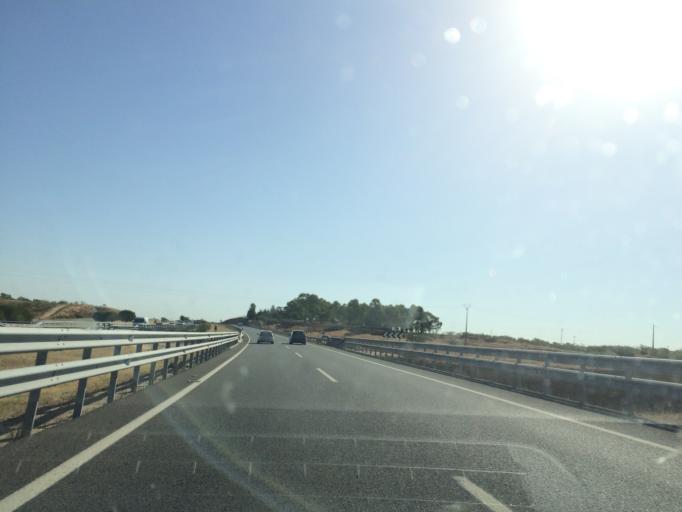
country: ES
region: Castille-La Mancha
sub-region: Province of Toledo
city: Valmojado
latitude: 40.2179
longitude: -4.0827
